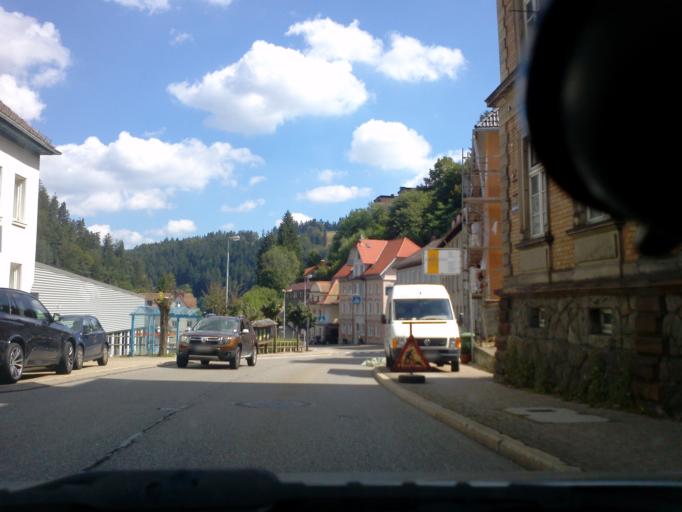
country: DE
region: Baden-Wuerttemberg
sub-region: Freiburg Region
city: Triberg im Schwarzwald
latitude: 48.1338
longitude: 8.2350
